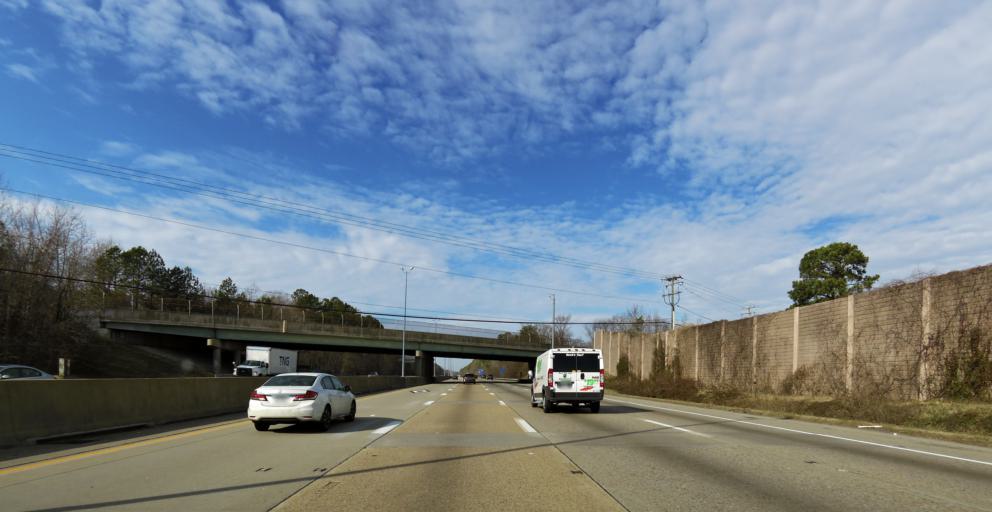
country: US
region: Virginia
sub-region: City of Newport News
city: Newport News
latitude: 37.0653
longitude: -76.4265
